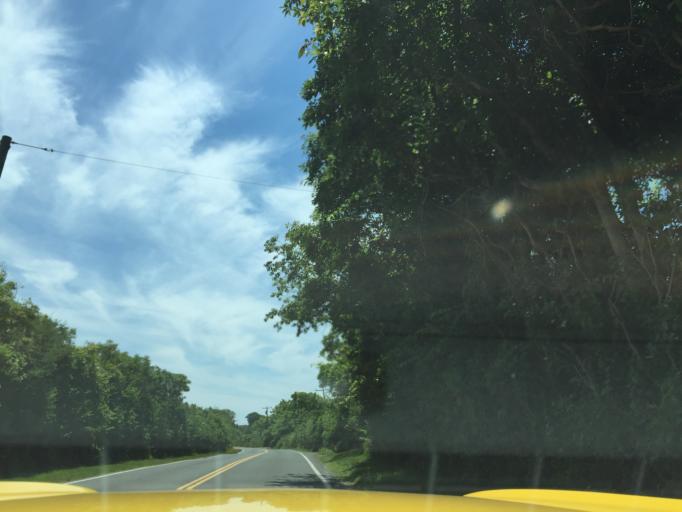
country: US
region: New York
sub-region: Suffolk County
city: Montauk
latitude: 41.0585
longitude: -71.9056
